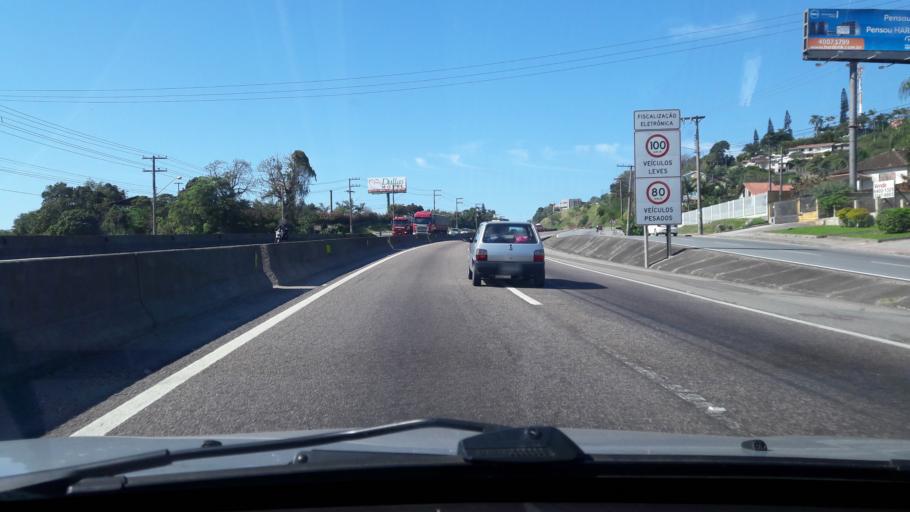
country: BR
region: Santa Catarina
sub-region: Biguacu
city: Biguacu
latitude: -27.5143
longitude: -48.6399
